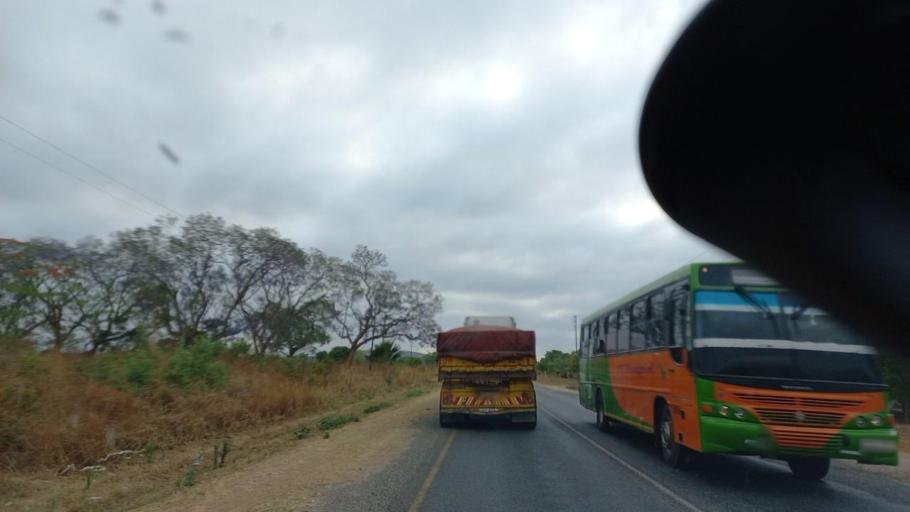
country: ZM
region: Lusaka
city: Chongwe
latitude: -15.3492
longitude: 28.5687
